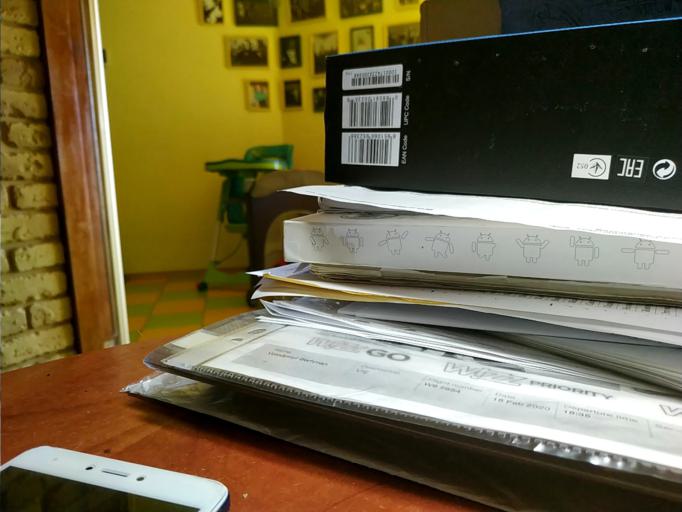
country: RU
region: Novgorod
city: Kholm
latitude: 59.2574
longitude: 32.8249
